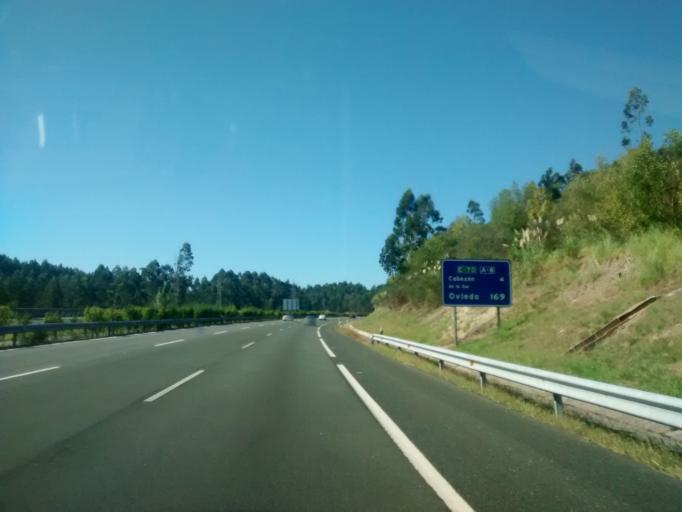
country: ES
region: Cantabria
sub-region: Provincia de Cantabria
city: Luzmela
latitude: 43.3229
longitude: -4.2034
